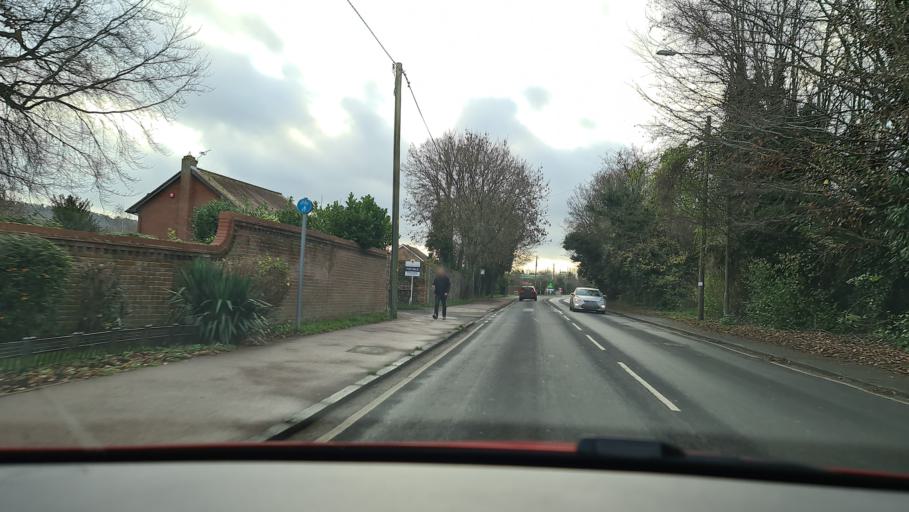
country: GB
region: England
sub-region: Buckinghamshire
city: Wendover
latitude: 51.7691
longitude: -0.7459
